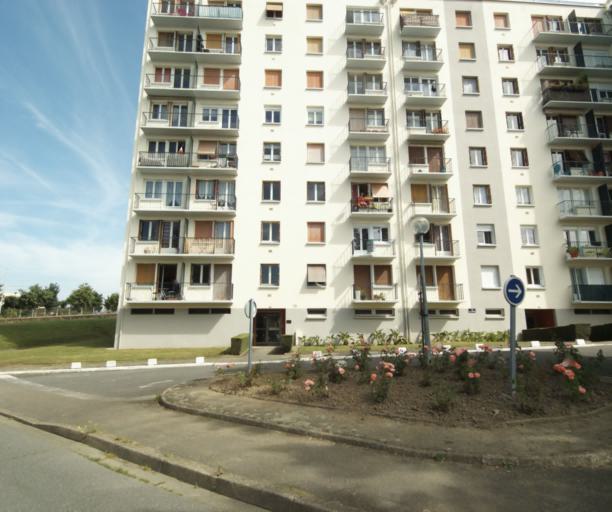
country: FR
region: Pays de la Loire
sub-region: Departement de la Mayenne
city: Laval
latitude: 48.0759
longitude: -0.7803
